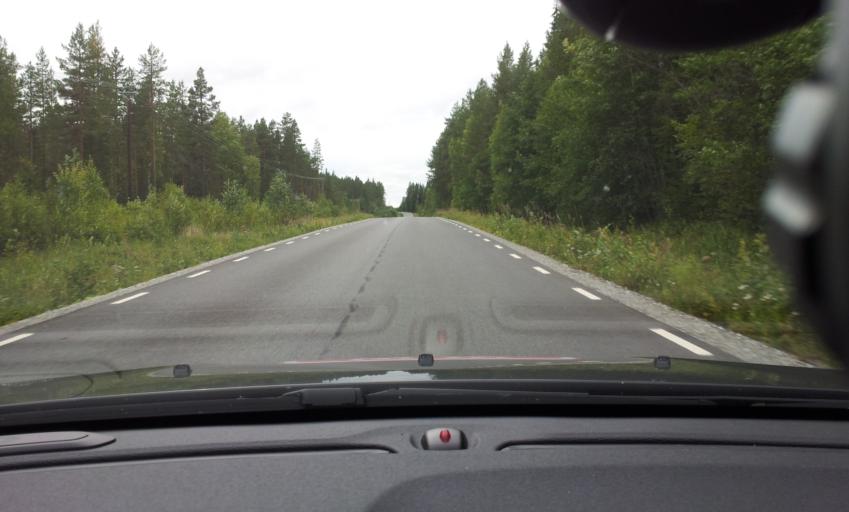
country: SE
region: Jaemtland
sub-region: Braecke Kommun
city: Braecke
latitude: 63.1389
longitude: 15.5289
